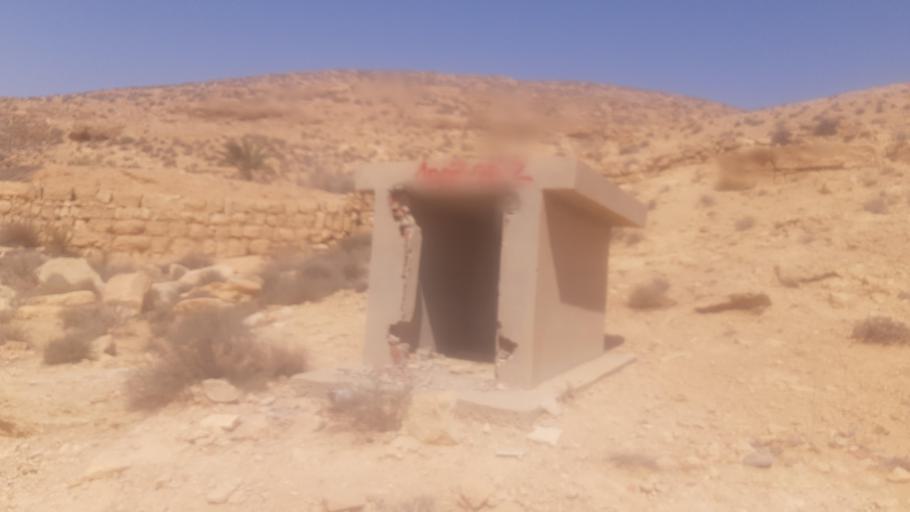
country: TN
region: Tataouine
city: Tataouine
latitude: 32.8924
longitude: 10.2313
